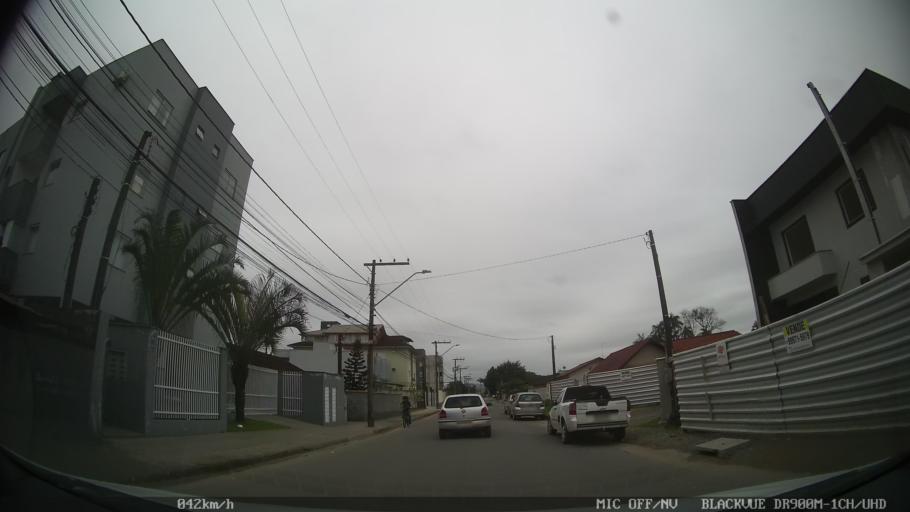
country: BR
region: Santa Catarina
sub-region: Joinville
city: Joinville
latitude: -26.2814
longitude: -48.9070
